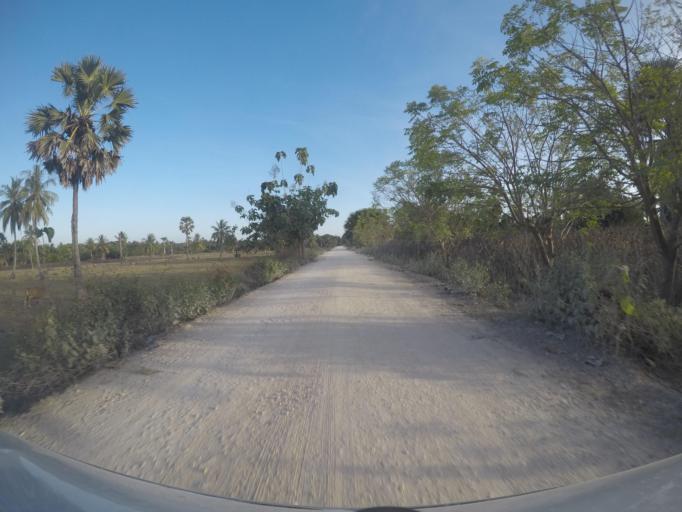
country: TL
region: Viqueque
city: Viqueque
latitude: -8.8876
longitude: 126.5070
